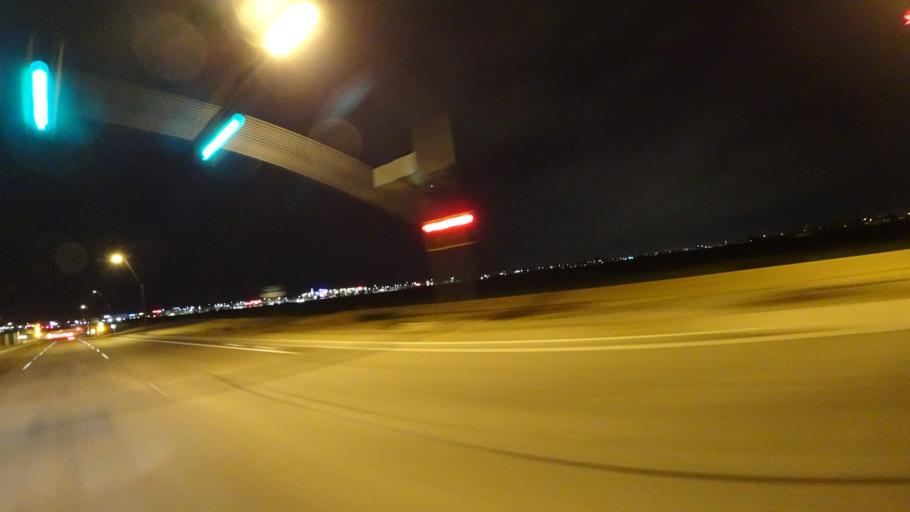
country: US
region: Arizona
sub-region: Maricopa County
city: Queen Creek
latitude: 33.2613
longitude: -111.6361
